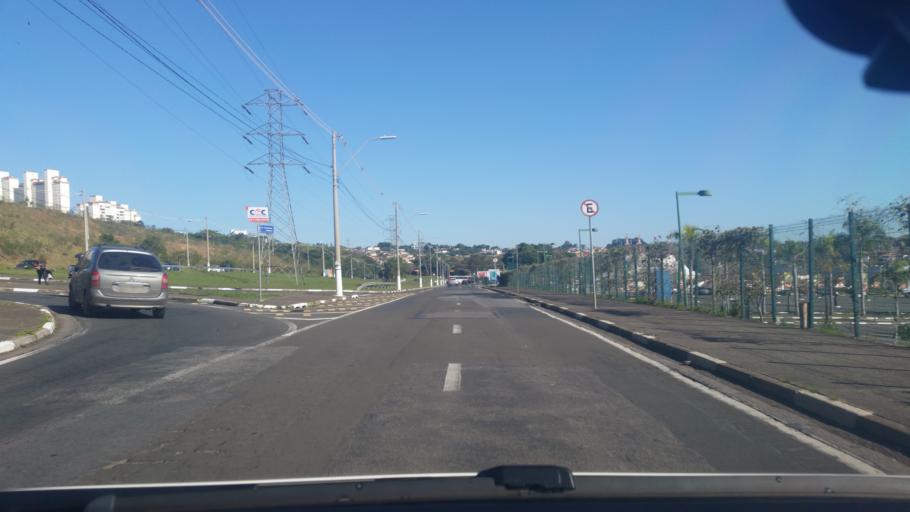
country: BR
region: Sao Paulo
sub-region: Campinas
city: Campinas
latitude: -22.8487
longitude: -47.0601
